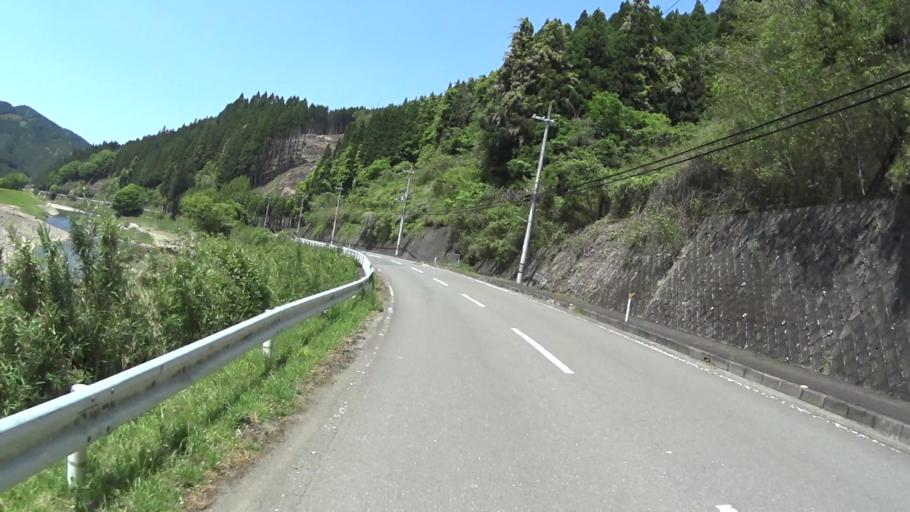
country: JP
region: Kyoto
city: Kameoka
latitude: 35.1381
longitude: 135.6027
